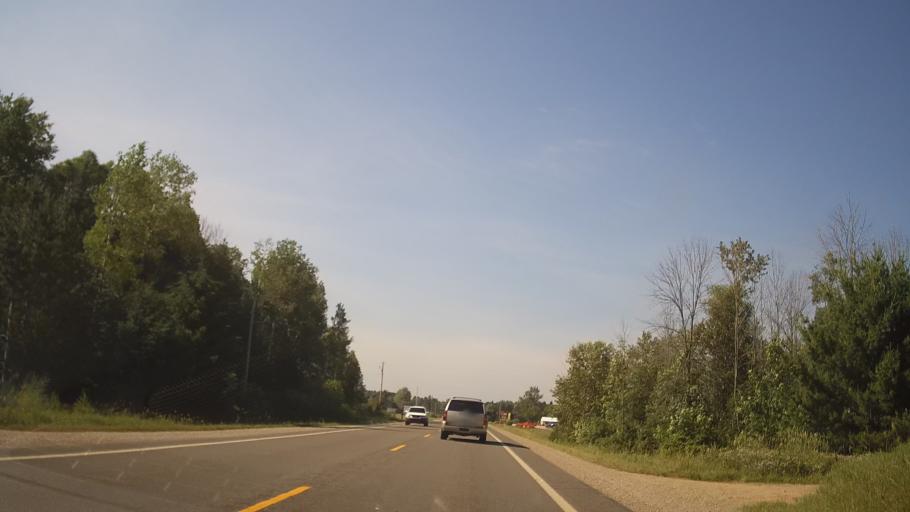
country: US
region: Michigan
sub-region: Ogemaw County
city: West Branch
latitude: 44.3252
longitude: -84.1257
